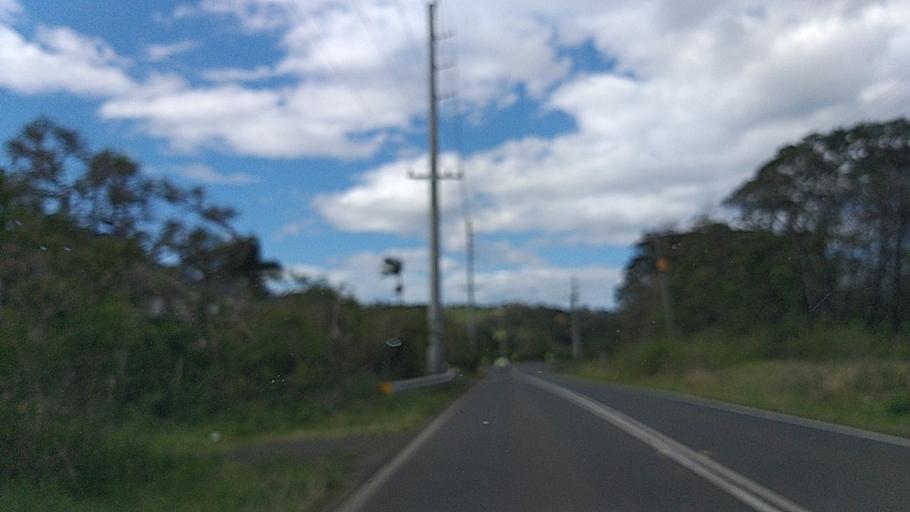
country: AU
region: New South Wales
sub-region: Wollongong
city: Dapto
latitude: -34.4700
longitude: 150.7949
